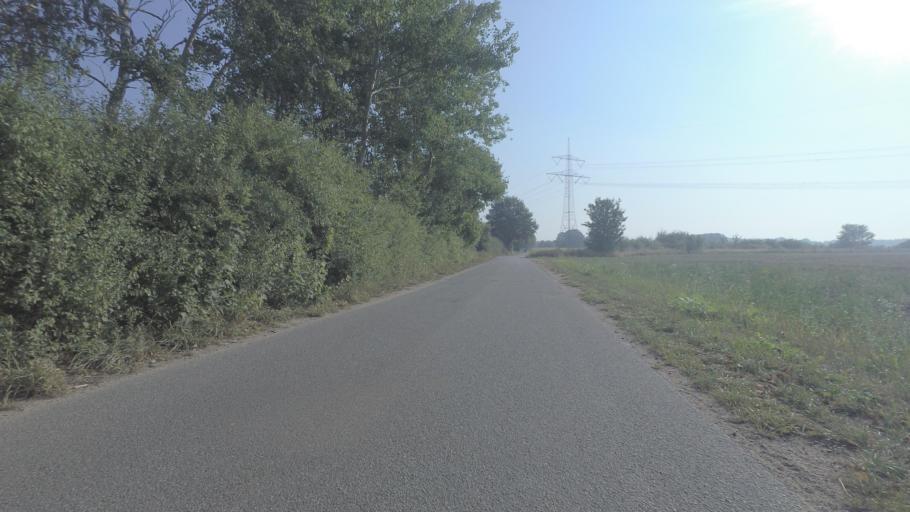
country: DE
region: Mecklenburg-Vorpommern
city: Malchow
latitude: 53.3562
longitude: 12.3680
